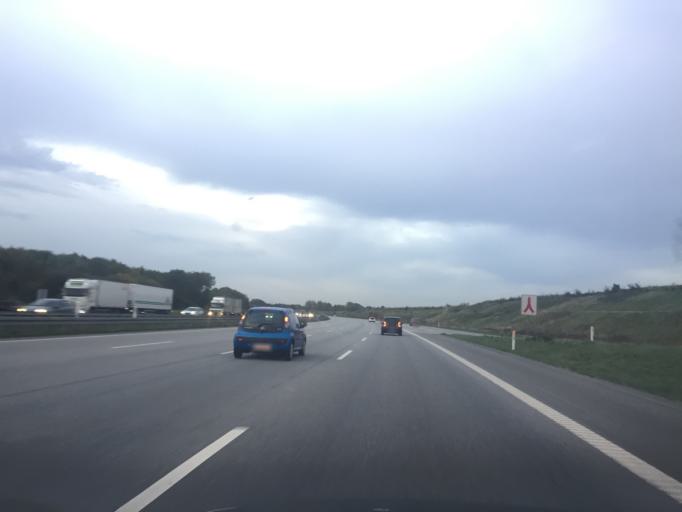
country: DK
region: Zealand
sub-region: Solrod Kommune
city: Solrod Strand
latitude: 55.5463
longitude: 12.2193
